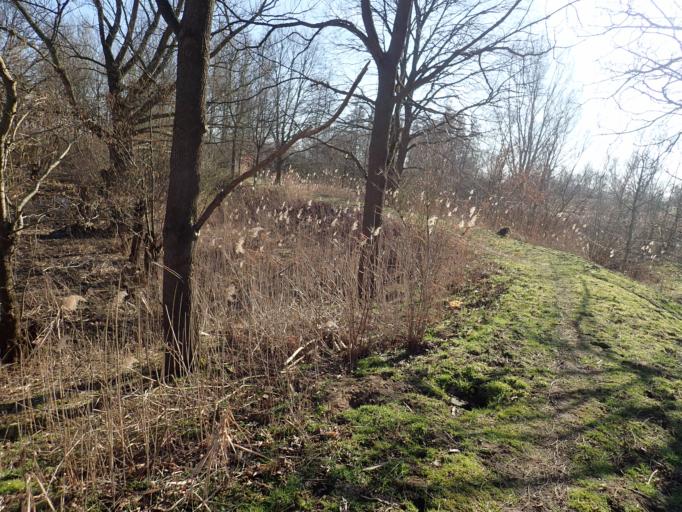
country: BE
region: Flanders
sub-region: Provincie Oost-Vlaanderen
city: Hamme
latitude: 51.0609
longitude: 4.1354
